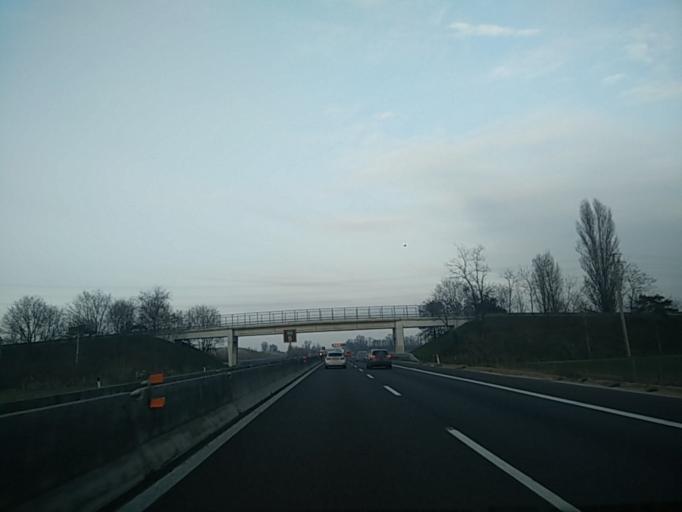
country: IT
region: Emilia-Romagna
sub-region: Provincia di Bologna
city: Progresso
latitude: 44.5751
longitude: 11.3895
